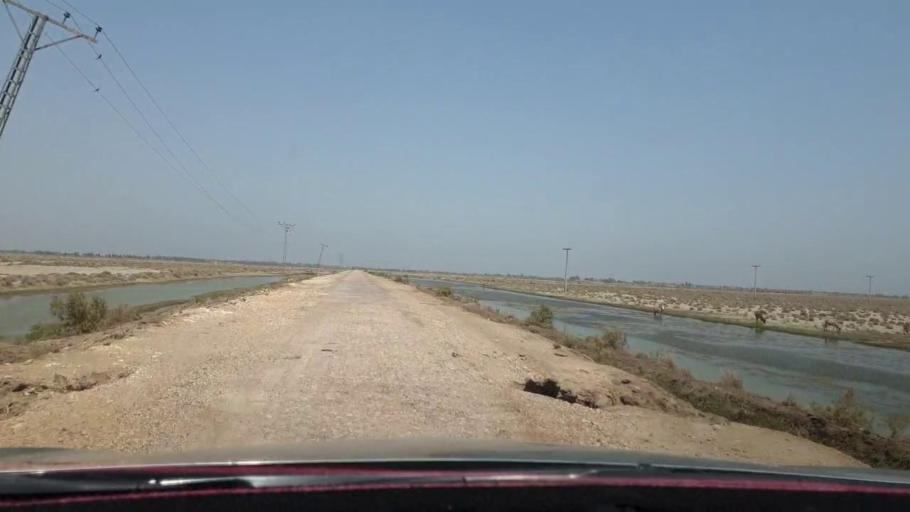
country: PK
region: Sindh
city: Warah
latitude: 27.3840
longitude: 67.6789
